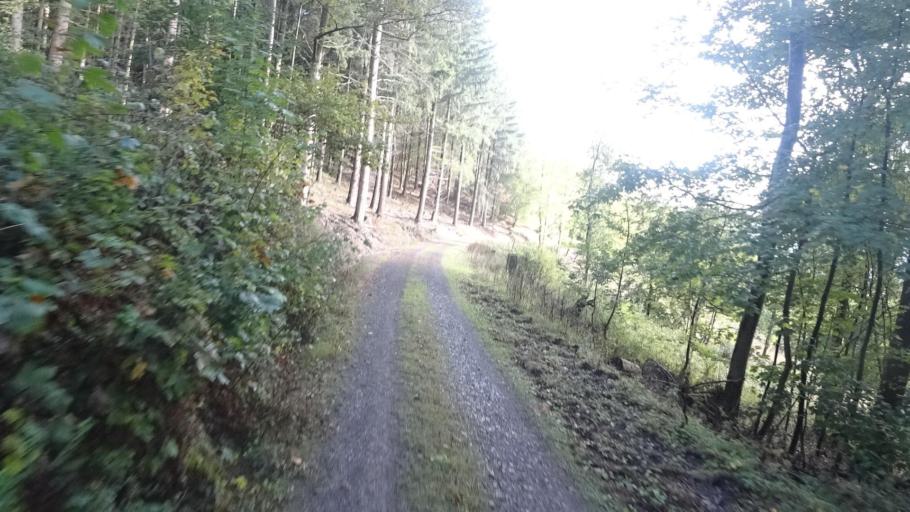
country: DE
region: Rheinland-Pfalz
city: Kamp-Bornhofen
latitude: 50.1959
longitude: 7.5972
